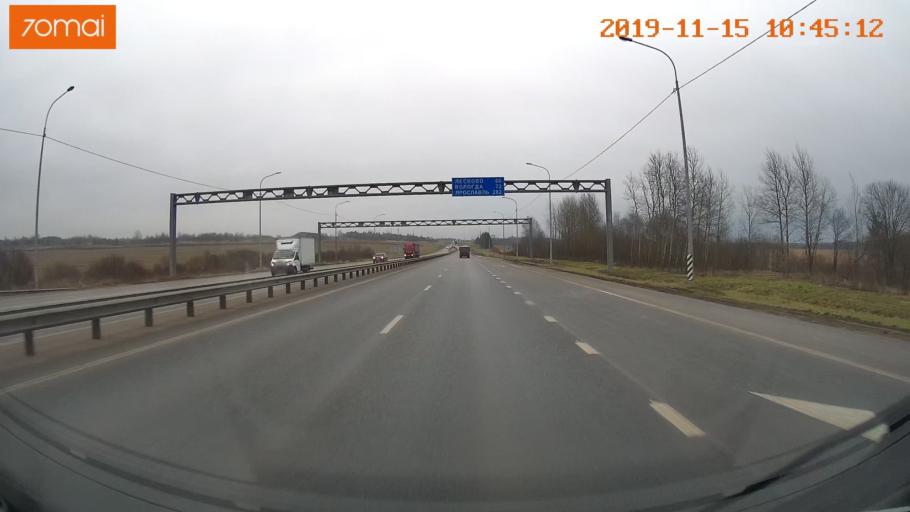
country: RU
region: Vologda
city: Sheksna
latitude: 59.2113
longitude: 38.5806
